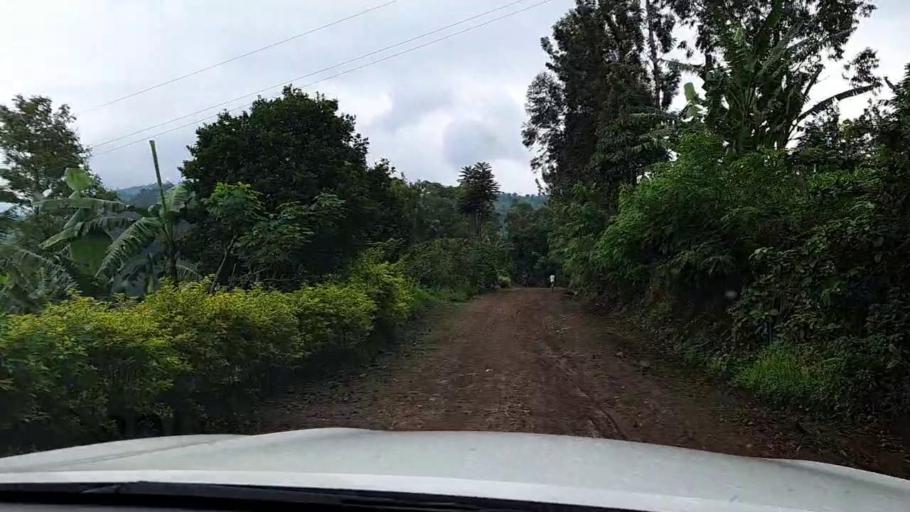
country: RW
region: Western Province
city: Cyangugu
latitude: -2.5456
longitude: 29.0377
